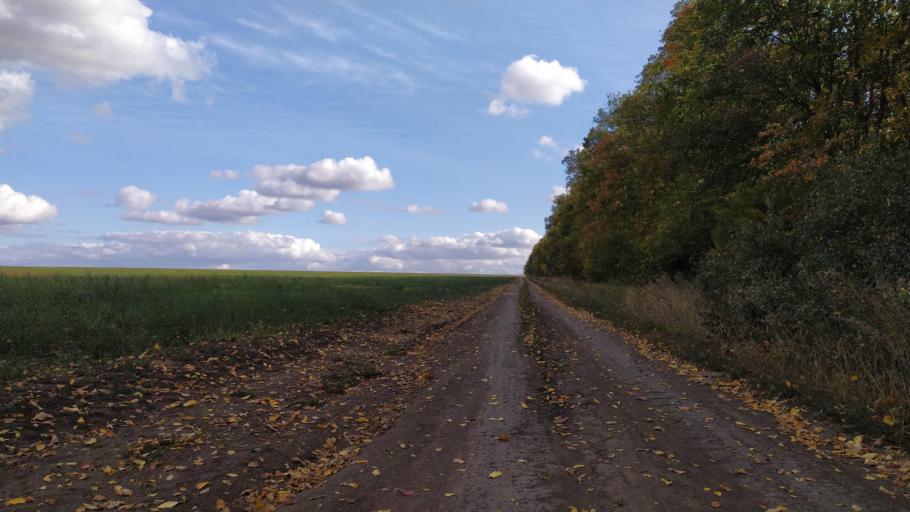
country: RU
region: Kursk
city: Kursk
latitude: 51.6217
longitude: 36.1616
